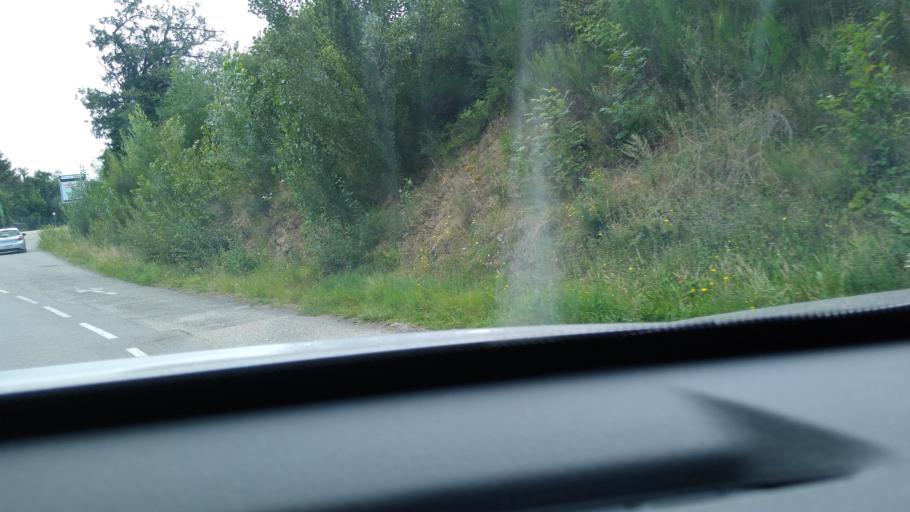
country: FR
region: Rhone-Alpes
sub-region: Departement de l'Ardeche
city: Davezieux
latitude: 45.2694
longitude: 4.7142
